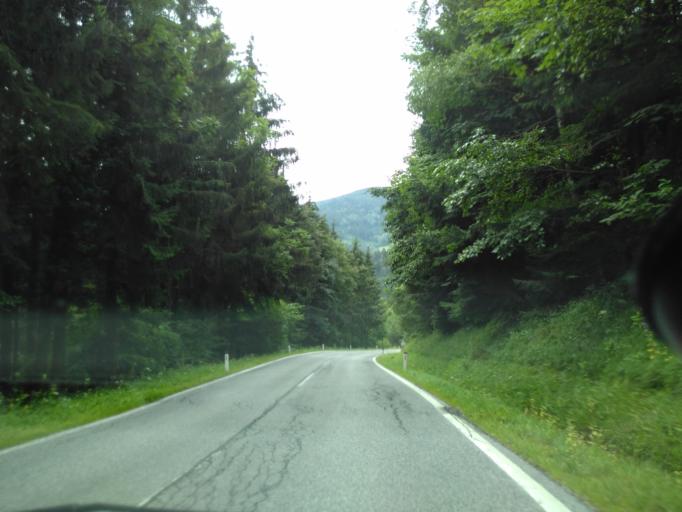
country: AT
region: Styria
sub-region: Politischer Bezirk Graz-Umgebung
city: Schrems bei Frohnleiten
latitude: 47.2771
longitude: 15.3904
